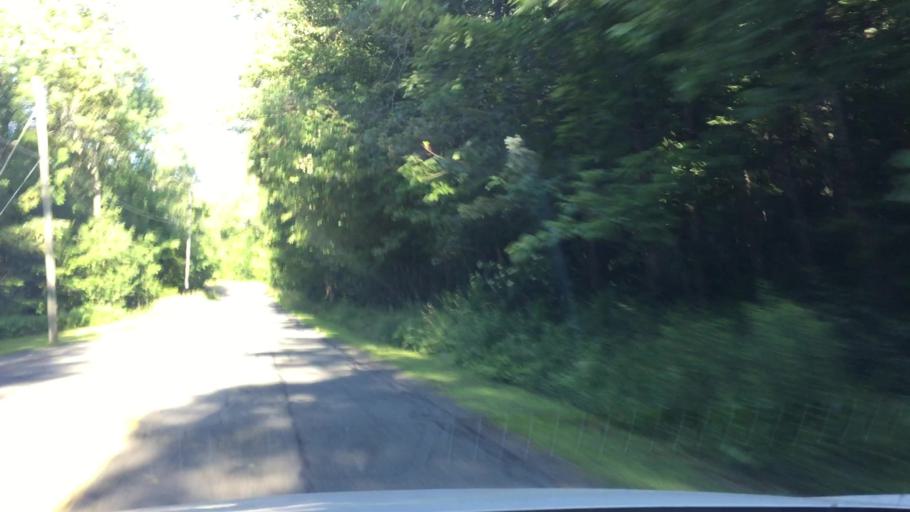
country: US
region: Massachusetts
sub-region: Berkshire County
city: Becket
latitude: 42.3171
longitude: -73.1128
